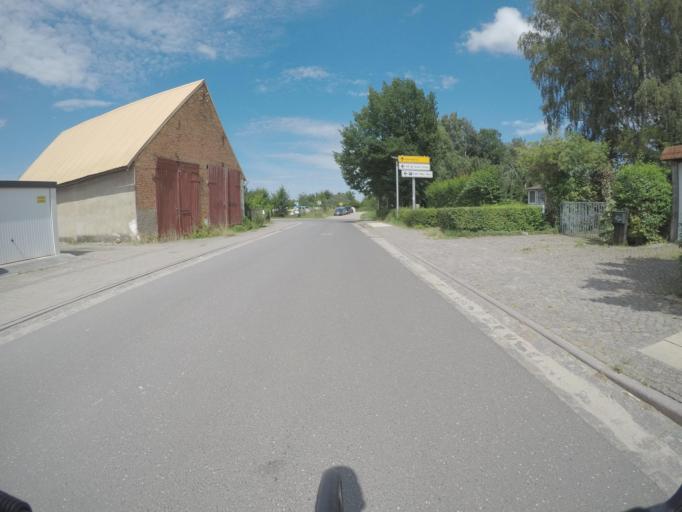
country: DE
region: Mecklenburg-Vorpommern
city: Altefahr
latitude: 54.3313
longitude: 13.1266
